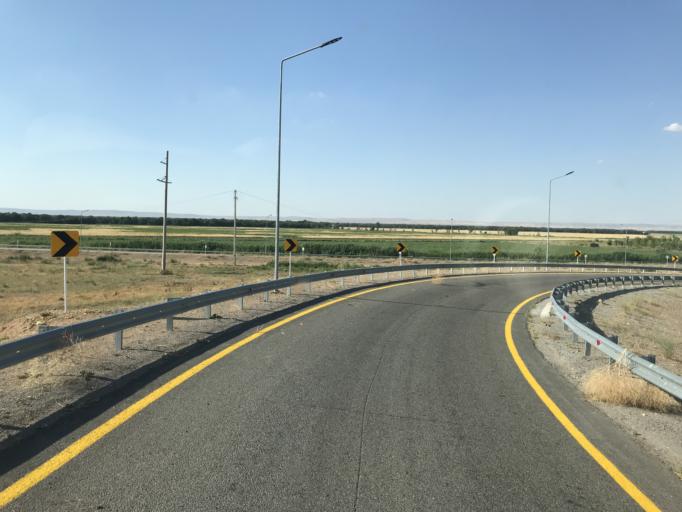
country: KG
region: Chuy
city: Sokuluk
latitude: 43.2762
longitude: 74.2294
